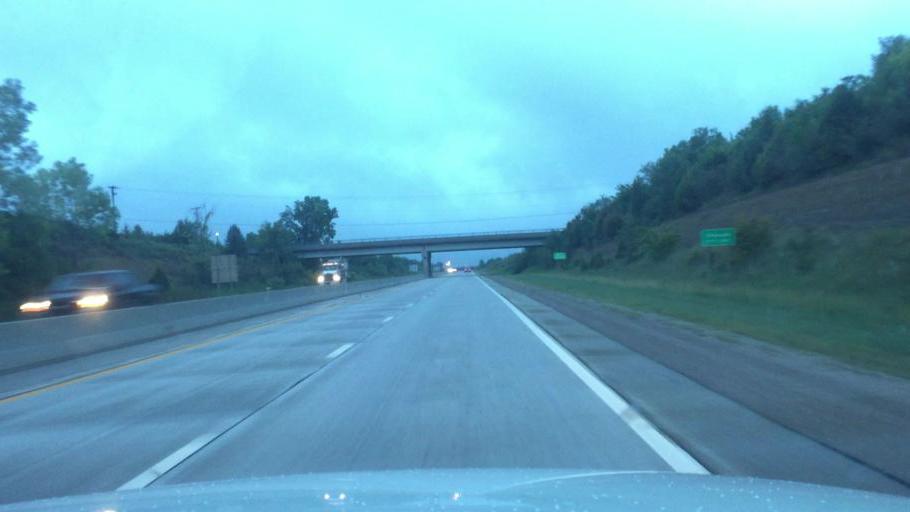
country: US
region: Kansas
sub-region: Neosho County
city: Chanute
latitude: 37.6764
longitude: -95.4796
